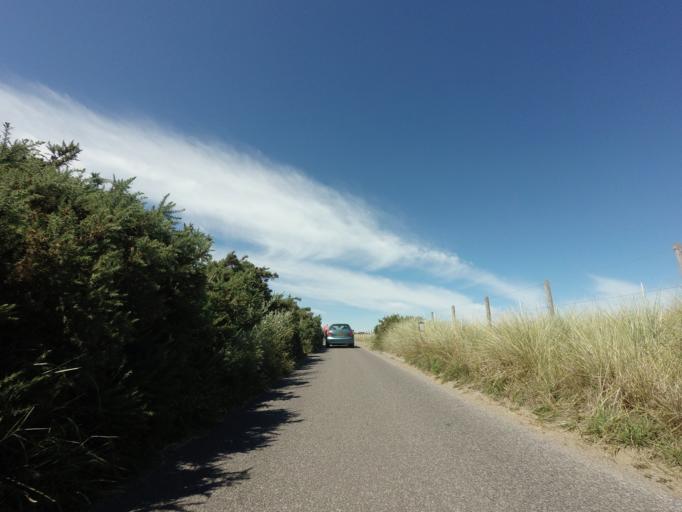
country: GB
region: England
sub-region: Kent
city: Deal
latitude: 51.2574
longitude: 1.3866
